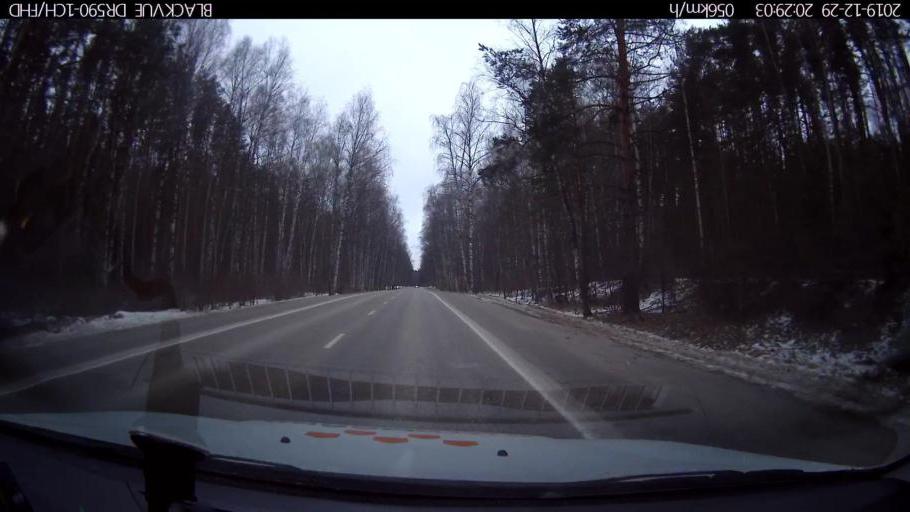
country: RU
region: Nizjnij Novgorod
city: Afonino
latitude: 56.1832
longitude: 44.1074
